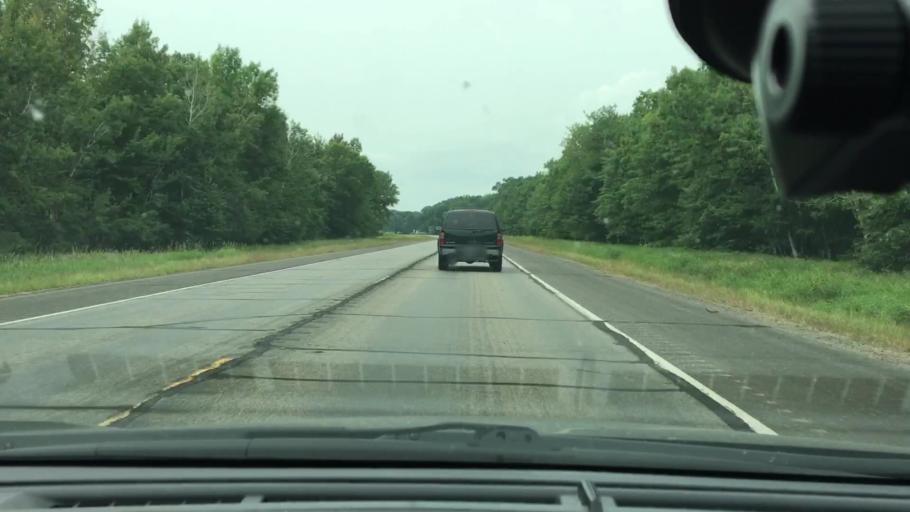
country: US
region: Minnesota
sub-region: Mille Lacs County
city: Vineland
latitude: 46.3246
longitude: -93.7953
